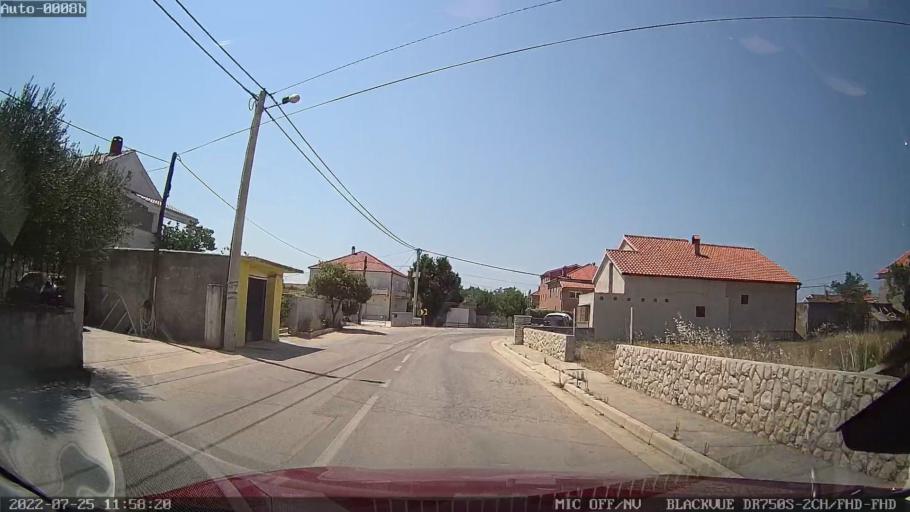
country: HR
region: Zadarska
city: Nin
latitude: 44.2387
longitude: 15.2116
